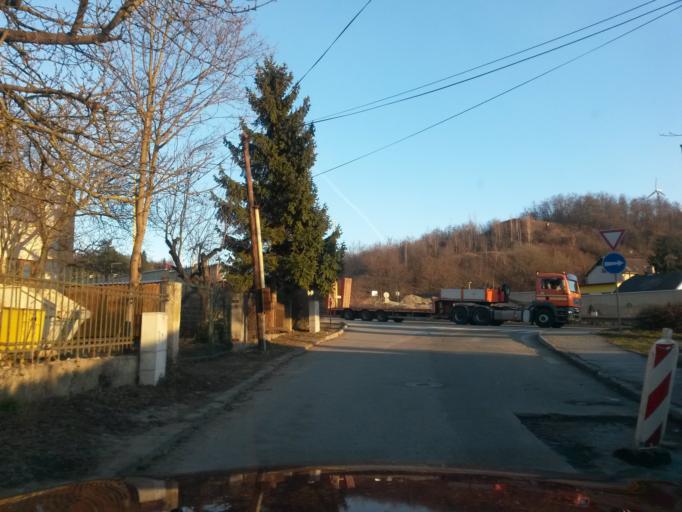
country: SK
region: Kosicky
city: Kosice
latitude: 48.7269
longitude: 21.2799
